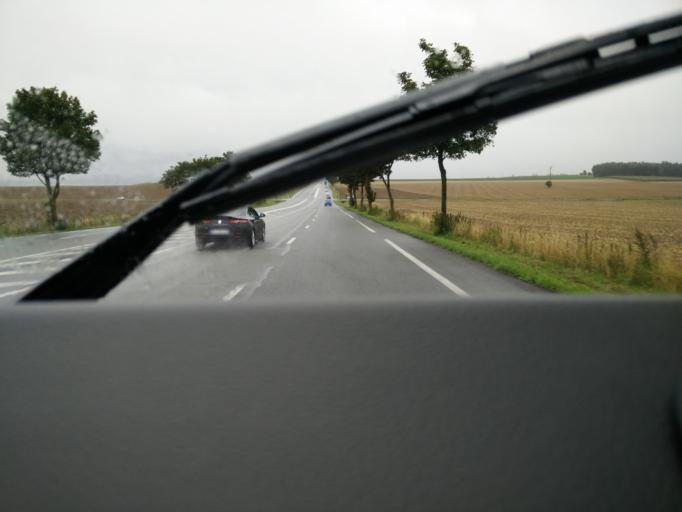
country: FR
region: Nord-Pas-de-Calais
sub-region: Departement du Pas-de-Calais
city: Saint-Pol-sur-Ternoise
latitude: 50.3866
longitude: 2.2487
